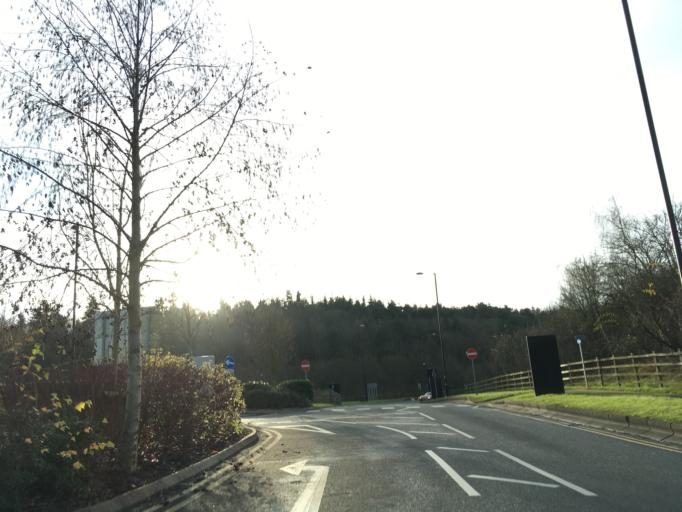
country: GB
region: England
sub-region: South Gloucestershire
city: Falfield
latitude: 51.6560
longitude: -2.4334
